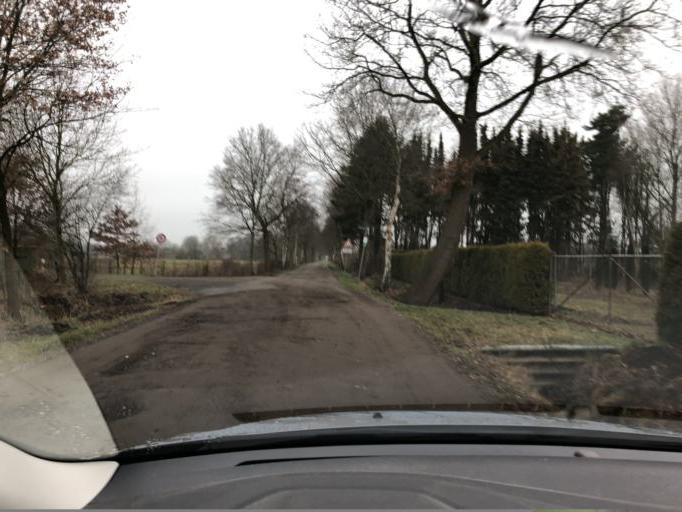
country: DE
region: Lower Saxony
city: Bad Zwischenahn
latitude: 53.1680
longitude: 8.0306
